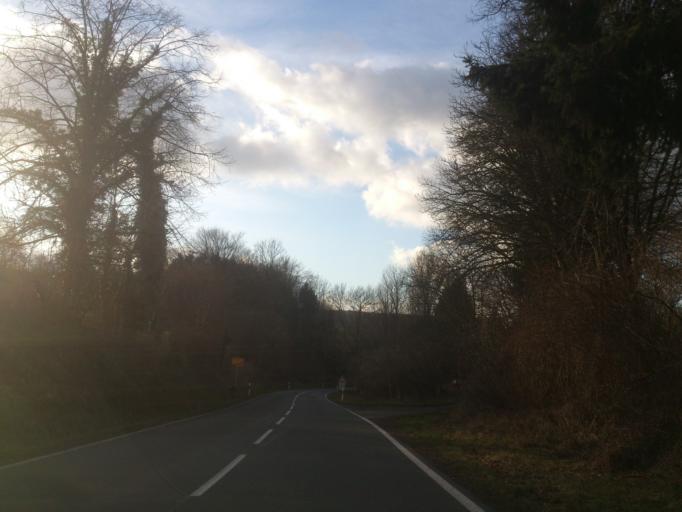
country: DE
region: Lower Saxony
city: Boffzen
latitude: 51.7502
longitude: 9.3012
